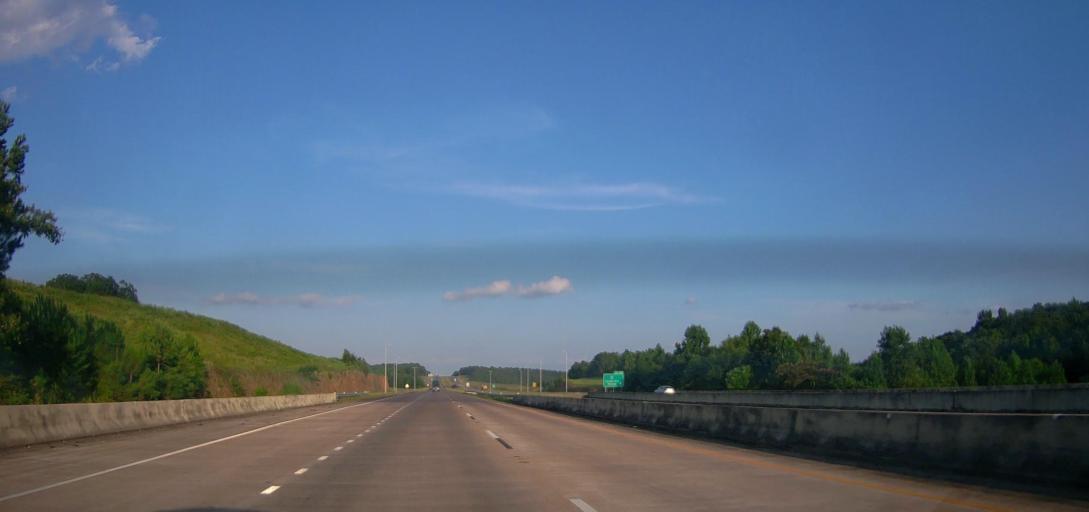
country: US
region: Alabama
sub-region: Walker County
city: Carbon Hill
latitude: 33.9148
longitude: -87.5097
